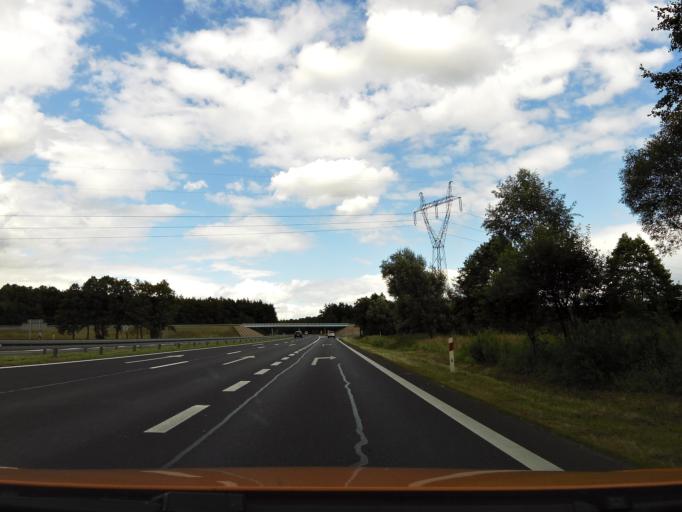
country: PL
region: West Pomeranian Voivodeship
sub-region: Powiat goleniowski
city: Goleniow
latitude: 53.5869
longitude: 14.8185
